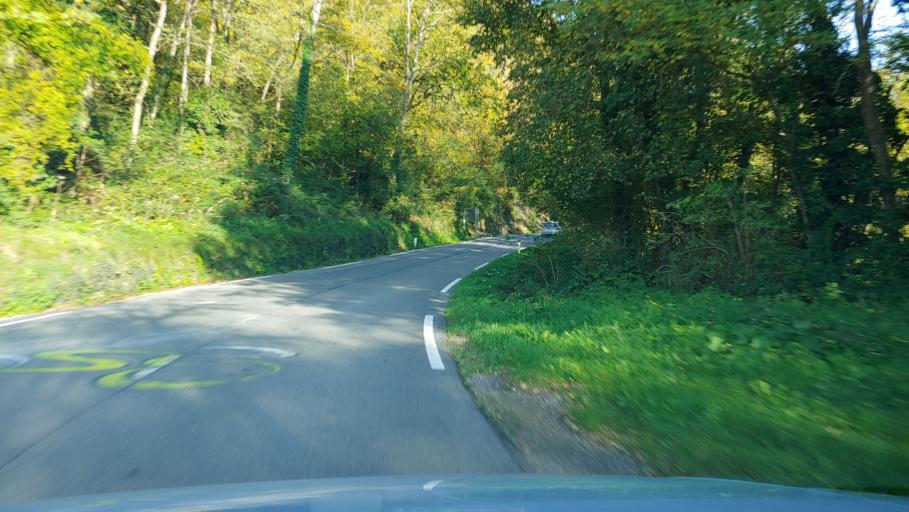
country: SI
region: Ajdovscina
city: Ajdovscina
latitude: 45.8136
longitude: 13.8918
